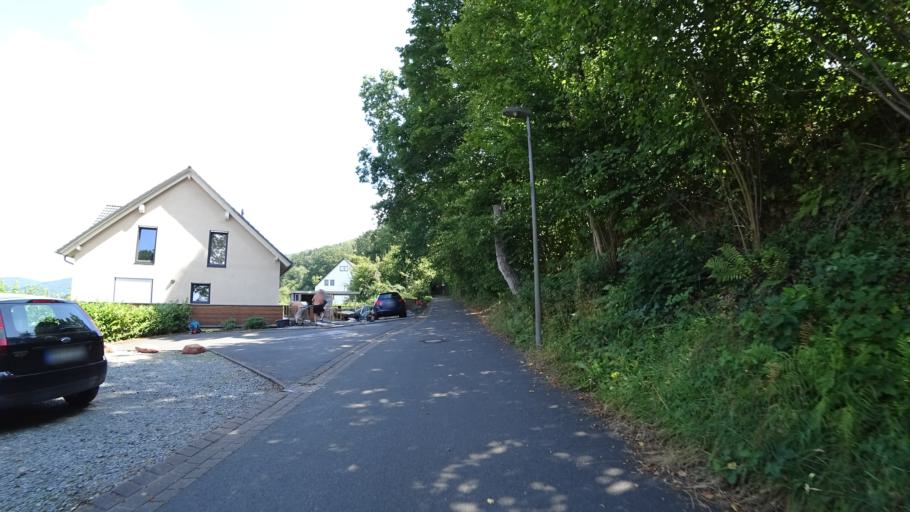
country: DE
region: Bavaria
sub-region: Regierungsbezirk Unterfranken
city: Miltenberg
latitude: 49.7033
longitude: 9.2786
